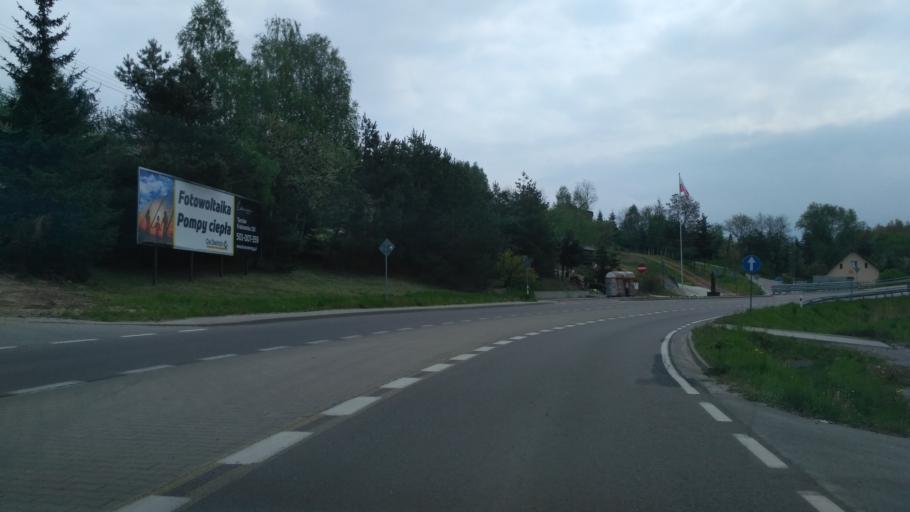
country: PL
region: Lesser Poland Voivodeship
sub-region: Powiat tarnowski
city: Tarnowiec
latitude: 49.9556
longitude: 21.0045
